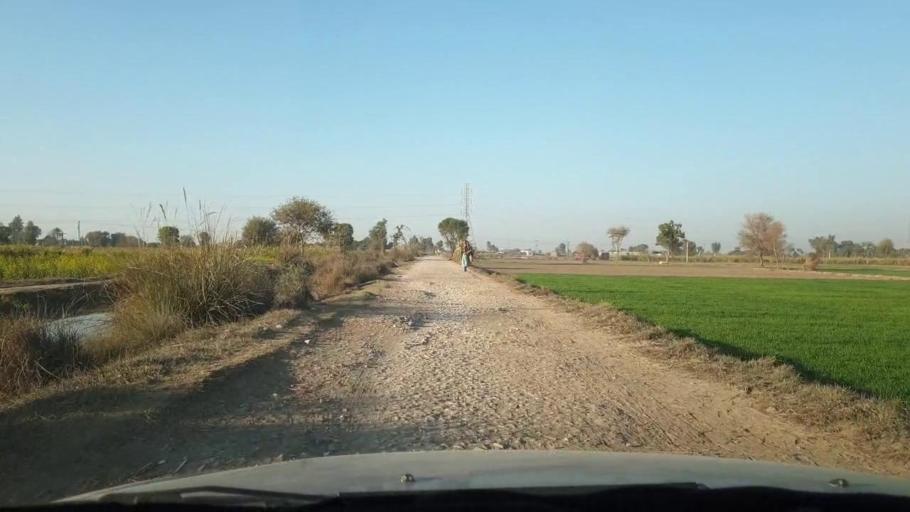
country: PK
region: Sindh
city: Ghotki
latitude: 27.9889
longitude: 69.2729
